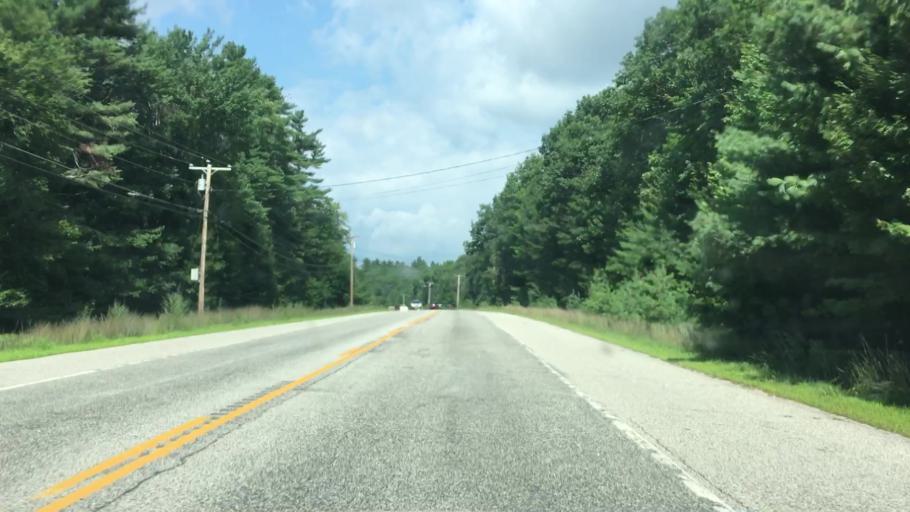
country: US
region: Maine
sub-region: Cumberland County
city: Raymond
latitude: 43.9055
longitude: -70.4858
